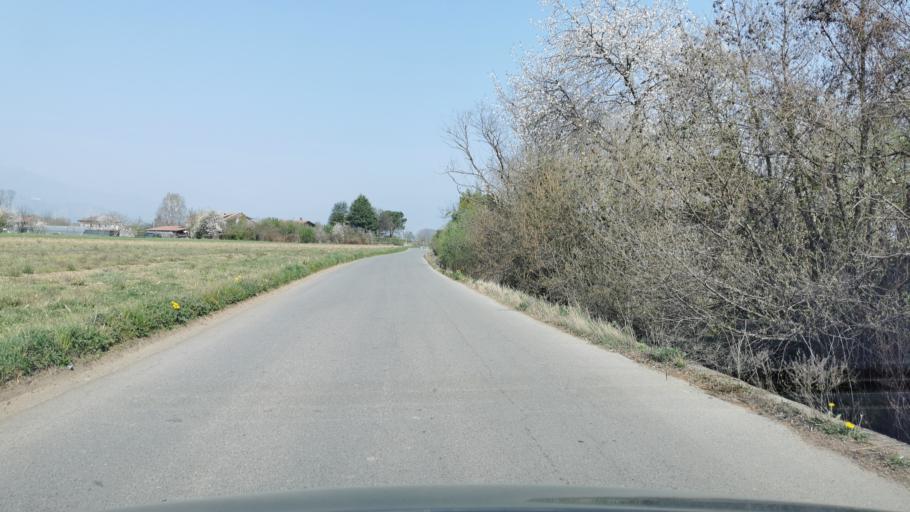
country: IT
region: Piedmont
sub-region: Provincia di Torino
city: Rivarolo Canavese
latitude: 45.3236
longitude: 7.7124
